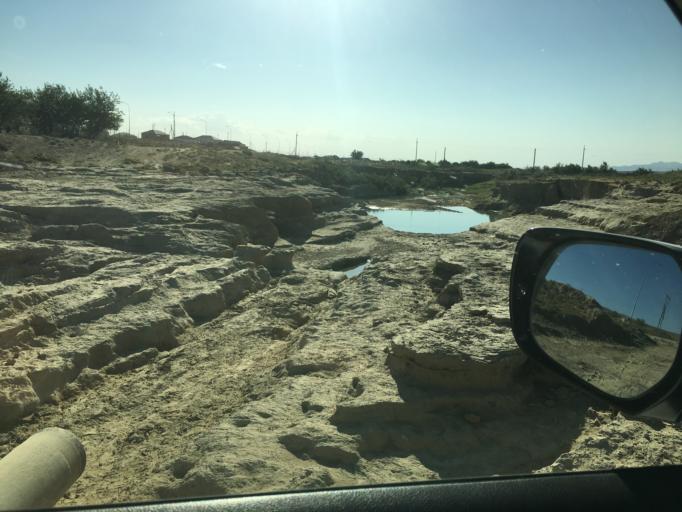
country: TM
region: Balkan
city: Magtymguly
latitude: 38.6307
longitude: 56.6198
